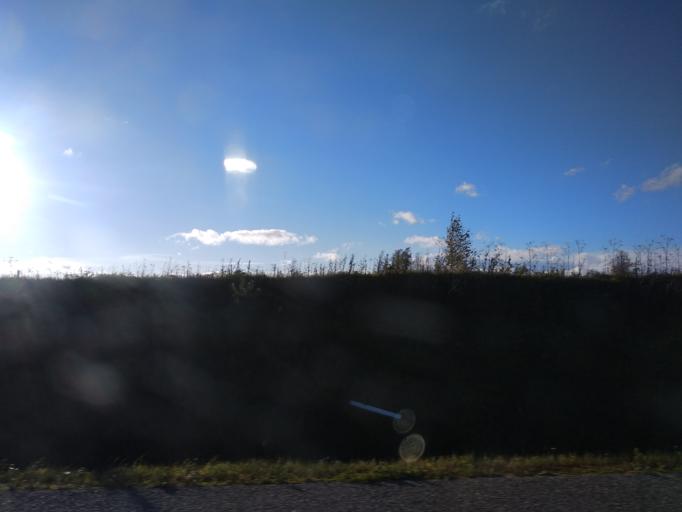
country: EE
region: Polvamaa
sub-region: Polva linn
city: Polva
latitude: 58.0174
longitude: 27.0617
